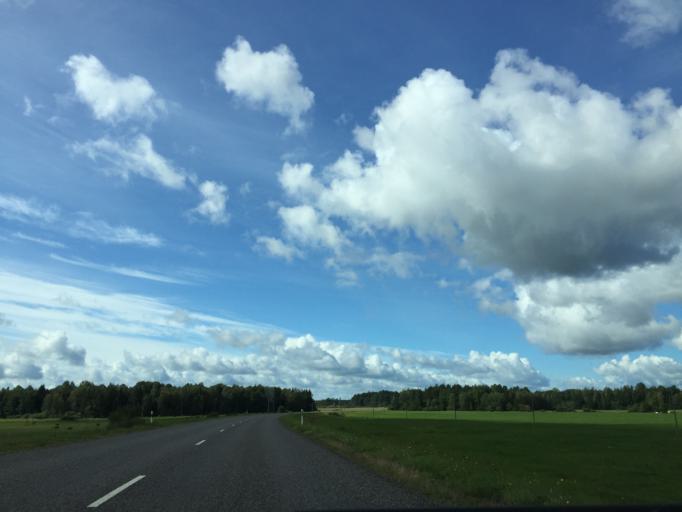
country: LV
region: Kuldigas Rajons
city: Kuldiga
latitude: 56.9978
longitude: 22.1274
